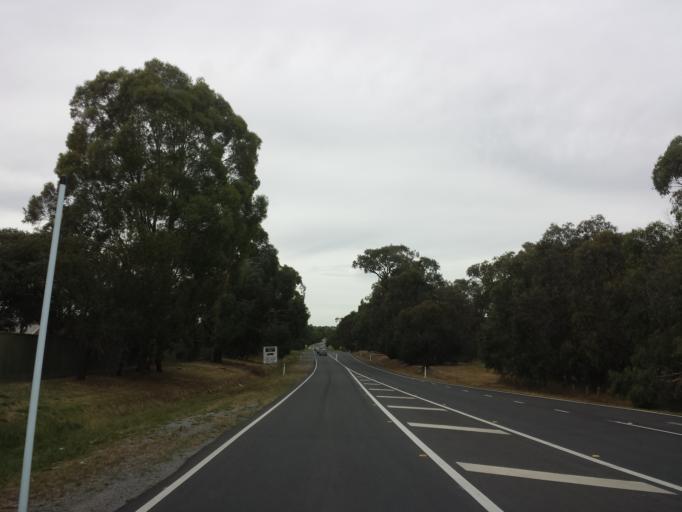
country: AU
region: Victoria
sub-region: Yarra Ranges
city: Lysterfield
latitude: -37.9192
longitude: 145.2707
